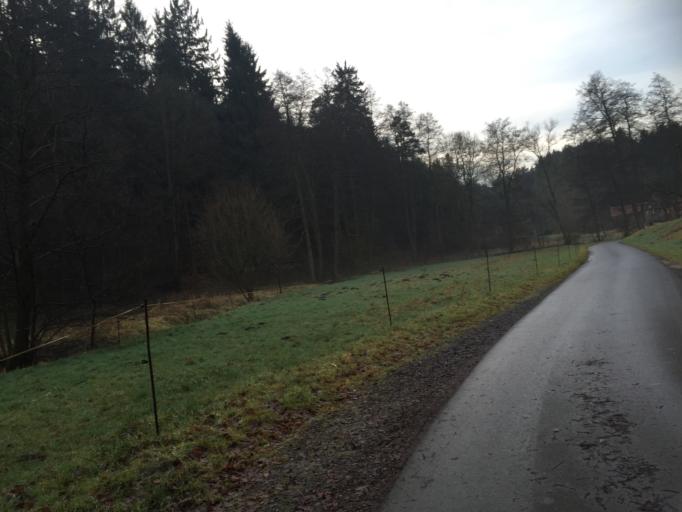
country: DE
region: Thuringia
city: Schleifreisen
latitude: 50.8886
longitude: 11.8136
